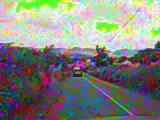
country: IE
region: Ulster
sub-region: County Donegal
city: Ramelton
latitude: 55.1975
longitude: -7.6389
